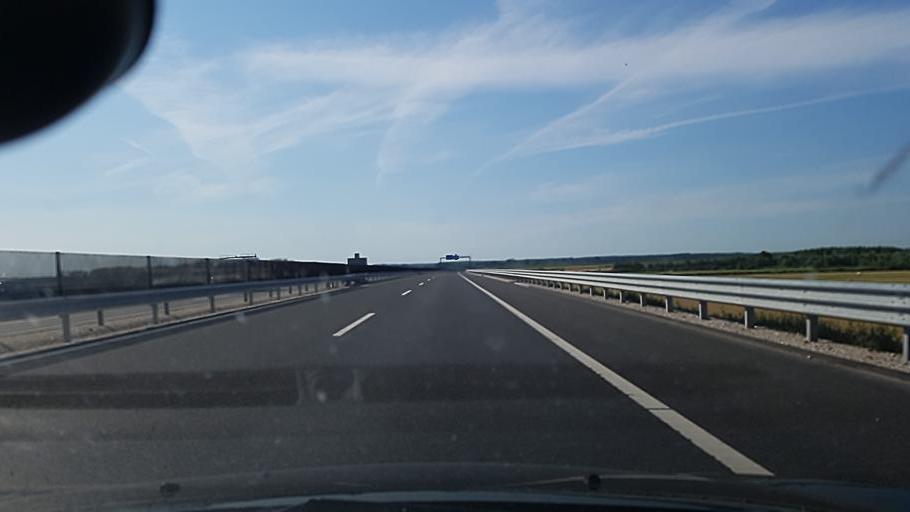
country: HU
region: Tolna
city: Tolna
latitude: 46.4031
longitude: 18.7448
